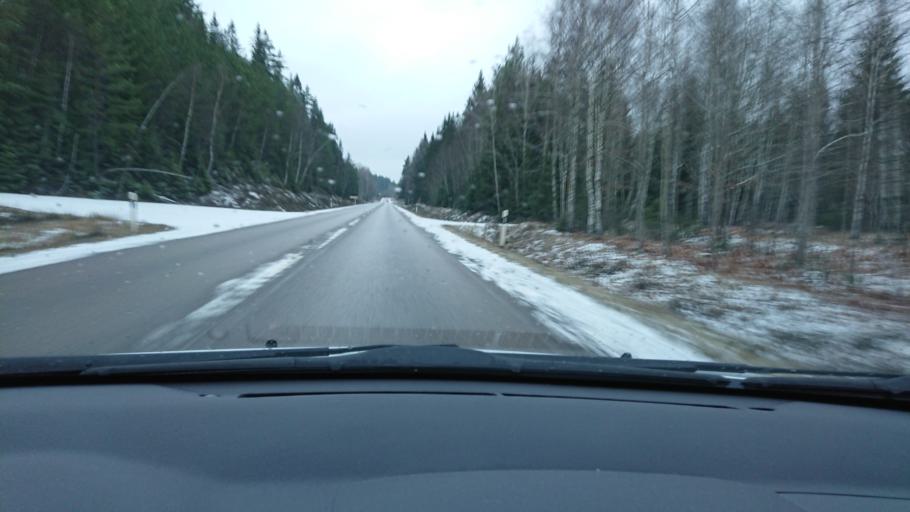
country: SE
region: Kalmar
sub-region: Hultsfreds Kommun
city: Hultsfred
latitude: 57.5452
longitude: 15.8460
